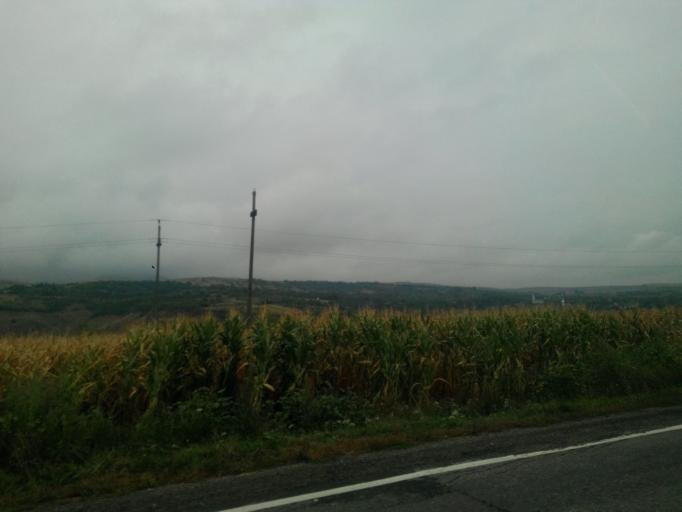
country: RO
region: Cluj
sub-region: Comuna Mihai Viteazu
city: Mihai Viteazu
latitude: 46.5297
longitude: 23.7081
